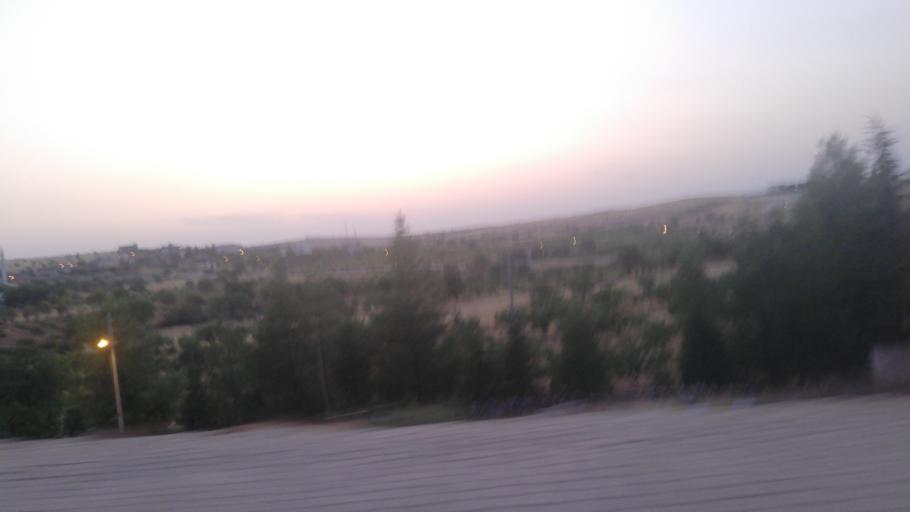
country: TR
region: Mardin
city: Kindirip
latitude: 37.4504
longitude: 41.2222
